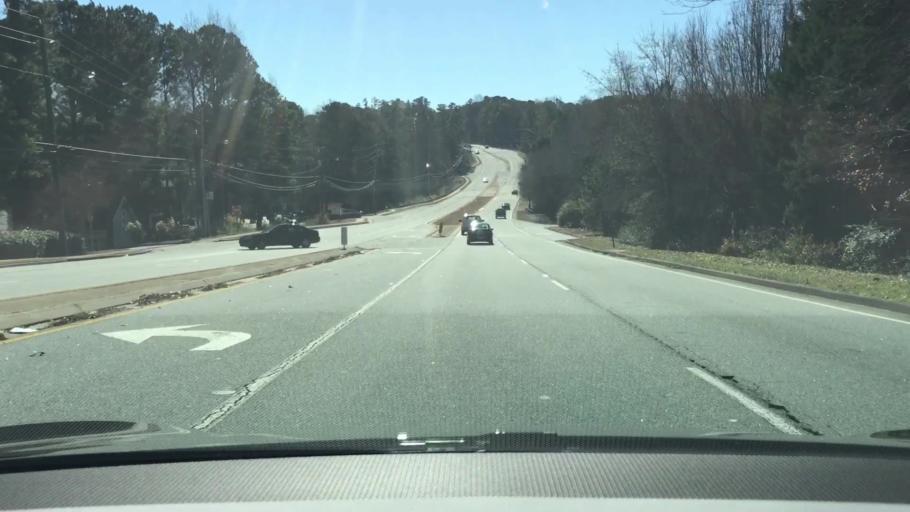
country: US
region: Georgia
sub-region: Gwinnett County
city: Lawrenceville
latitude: 33.9805
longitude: -84.0205
